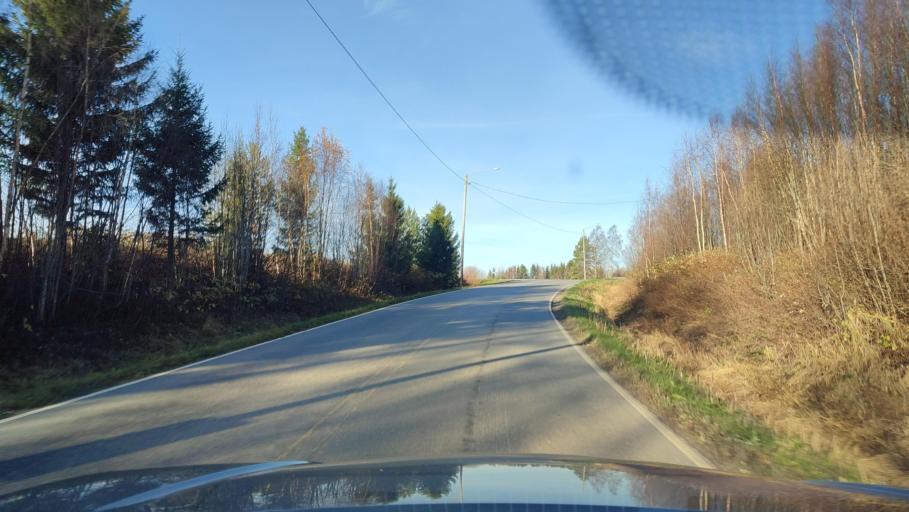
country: FI
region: Southern Ostrobothnia
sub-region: Suupohja
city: Karijoki
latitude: 62.2712
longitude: 21.7097
